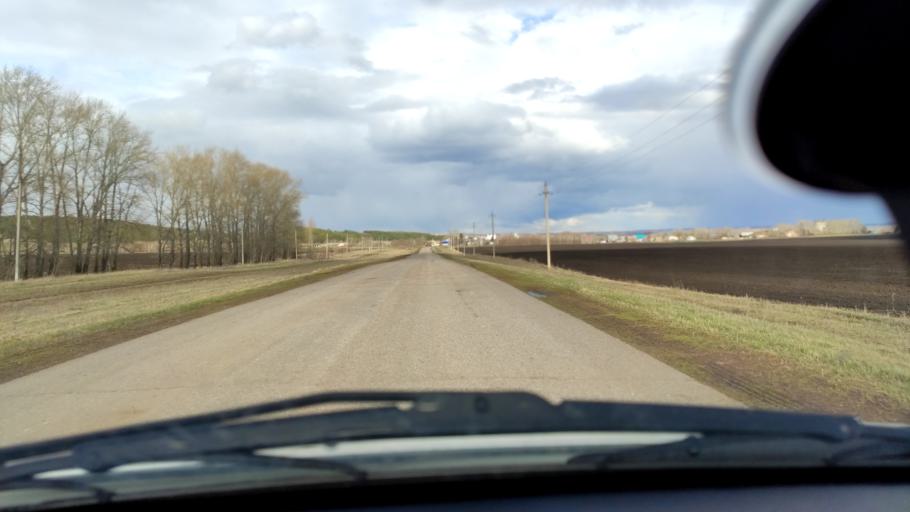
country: RU
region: Bashkortostan
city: Buzdyak
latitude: 54.7653
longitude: 54.5886
